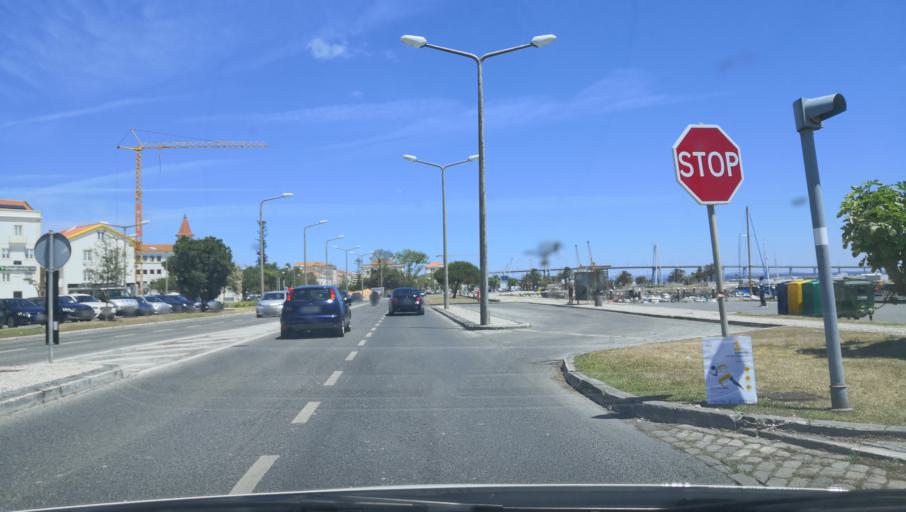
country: PT
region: Coimbra
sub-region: Figueira da Foz
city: Figueira da Foz
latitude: 40.1484
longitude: -8.8598
